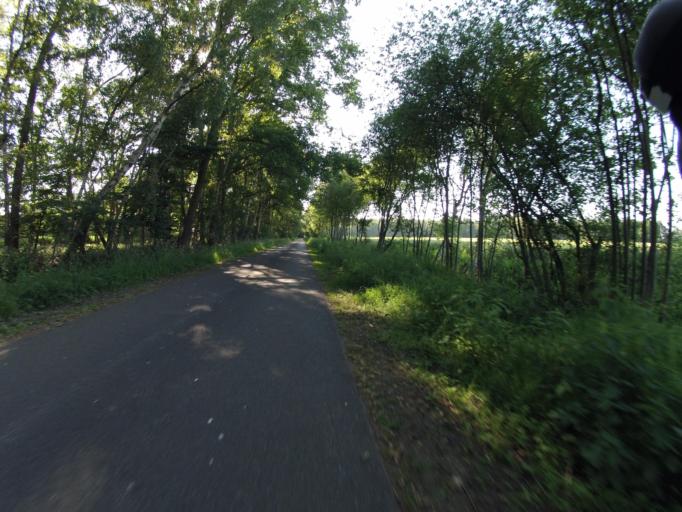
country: DE
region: Lower Saxony
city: Ohne
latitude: 52.3072
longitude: 7.3035
